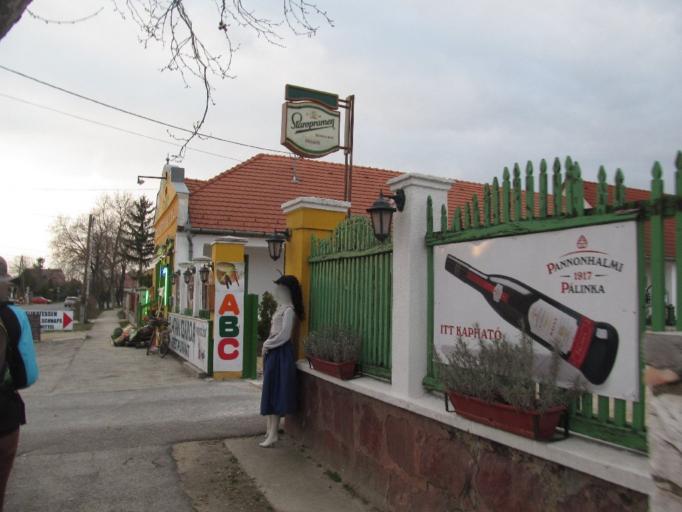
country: HU
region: Gyor-Moson-Sopron
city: Nyul
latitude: 47.5913
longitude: 17.6882
